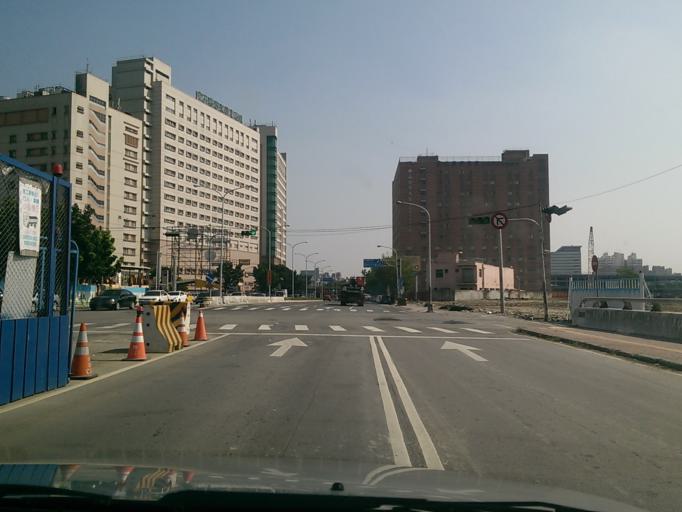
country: TW
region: Taiwan
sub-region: Taichung City
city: Taichung
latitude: 24.1231
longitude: 120.6482
